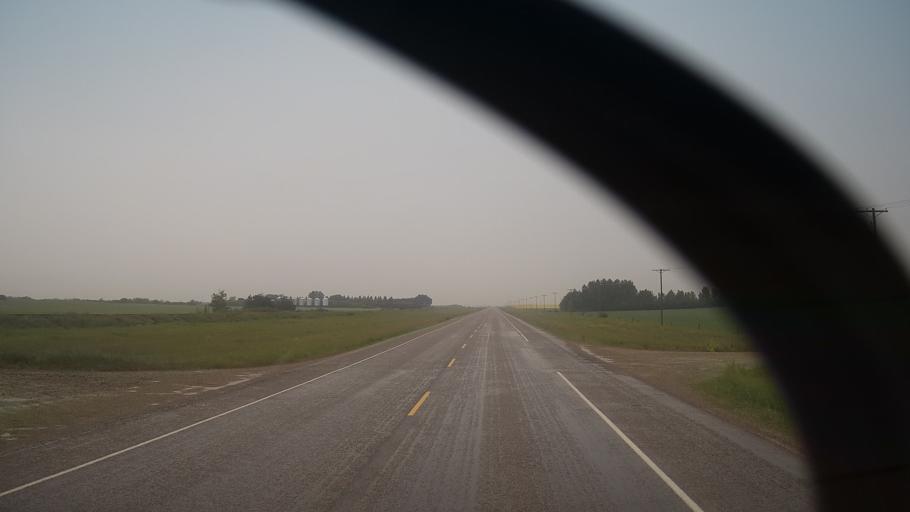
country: CA
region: Saskatchewan
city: Biggar
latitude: 52.1360
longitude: -108.1689
